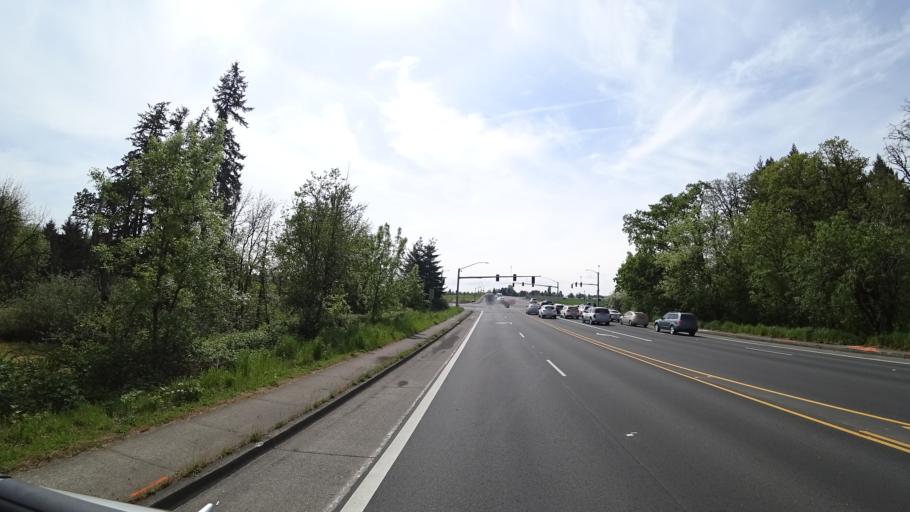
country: US
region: Oregon
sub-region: Washington County
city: Hillsboro
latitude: 45.5329
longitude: -122.9369
